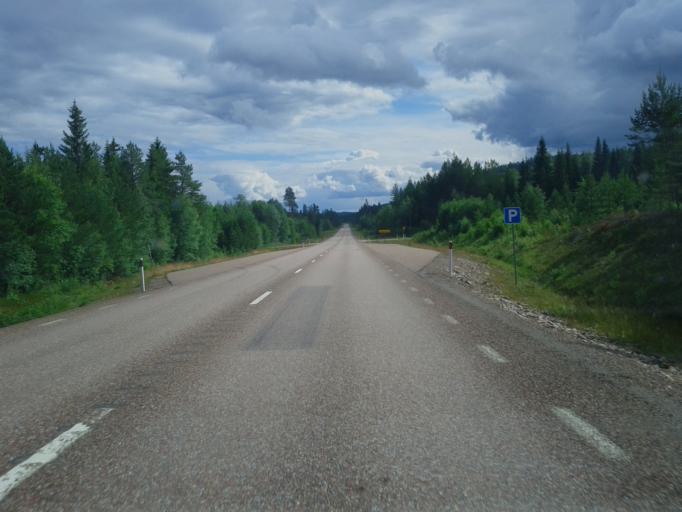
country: SE
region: Dalarna
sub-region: Rattviks Kommun
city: Raettvik
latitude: 60.8179
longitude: 15.2583
